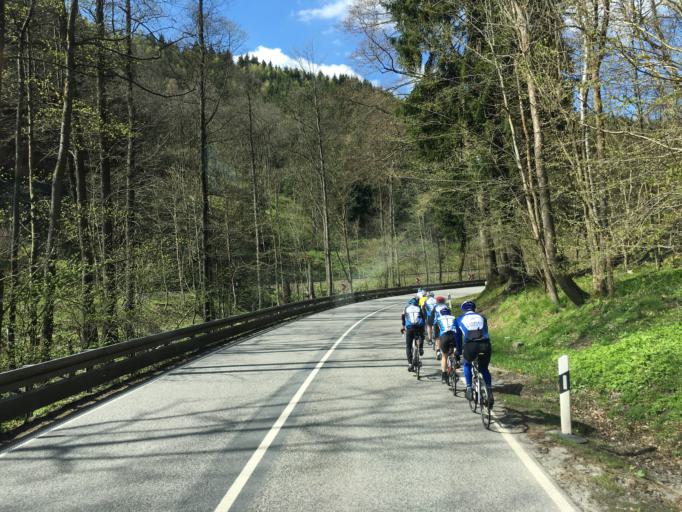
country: DE
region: Thuringia
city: Ilfeld
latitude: 51.6302
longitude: 10.8177
